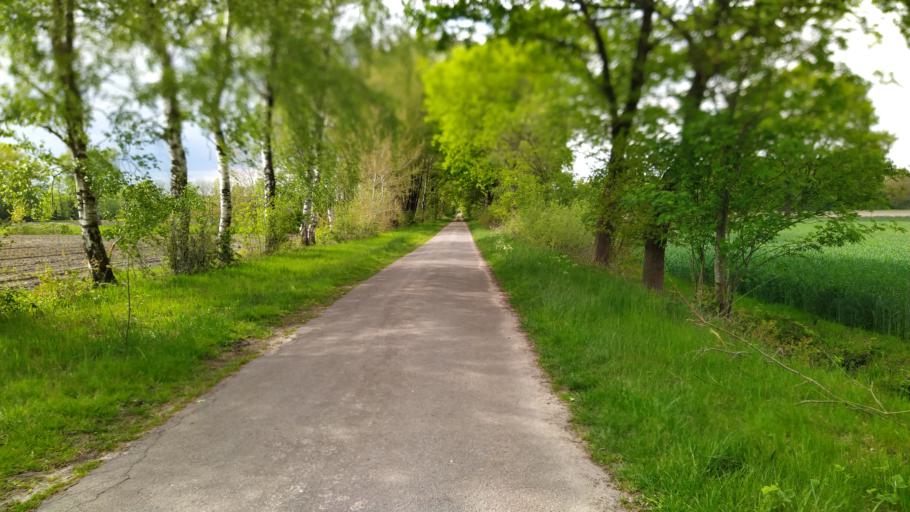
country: DE
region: Lower Saxony
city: Farven
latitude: 53.4292
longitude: 9.3383
